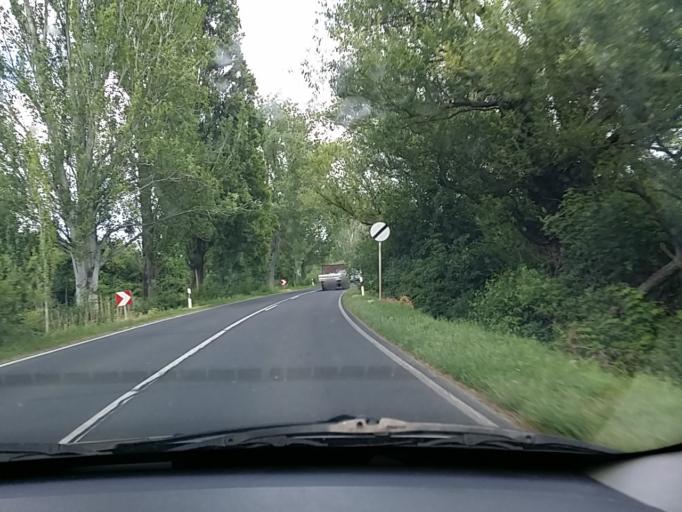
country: HU
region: Veszprem
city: Revfueloep
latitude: 46.8453
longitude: 17.6537
